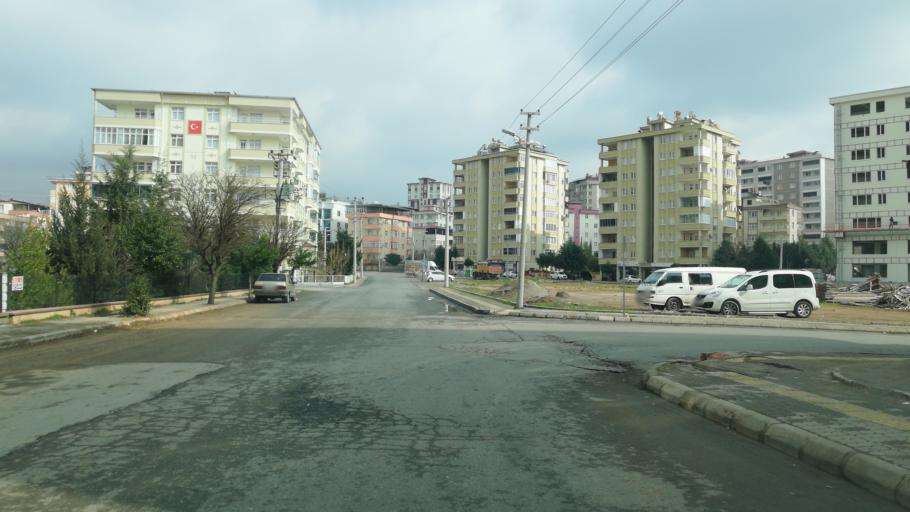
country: TR
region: Kahramanmaras
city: Kahramanmaras
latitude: 37.5830
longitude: 36.8979
